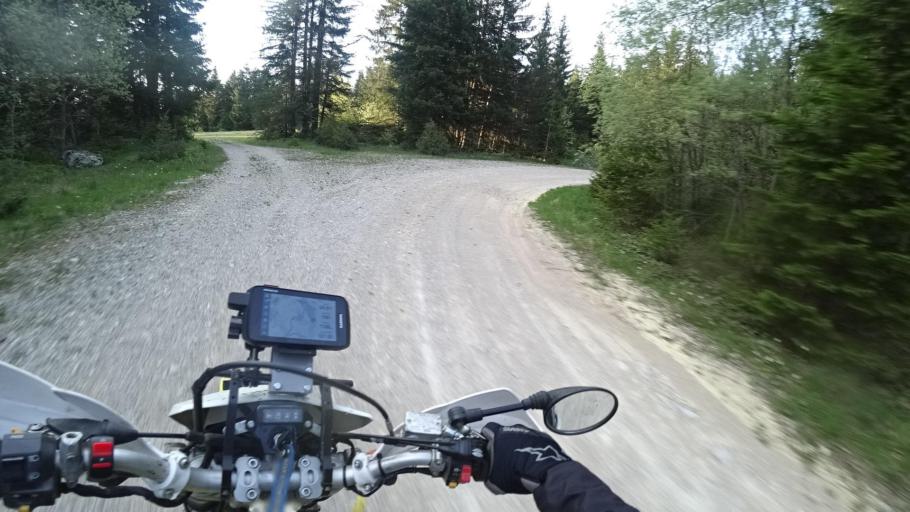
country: BA
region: Federation of Bosnia and Herzegovina
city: Rumboci
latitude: 43.7347
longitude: 17.5218
